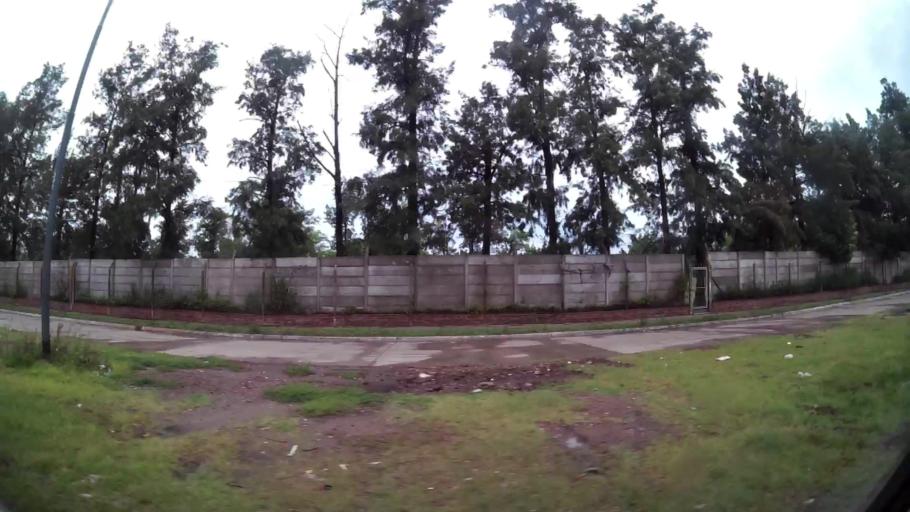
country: AR
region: Buenos Aires F.D.
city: Villa Lugano
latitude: -34.6556
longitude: -58.4502
